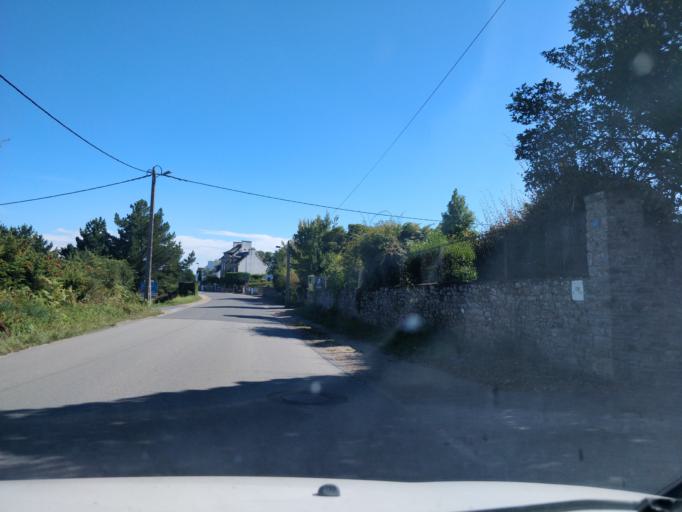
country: FR
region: Brittany
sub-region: Departement du Morbihan
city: Locmariaquer
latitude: 47.5739
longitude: -2.9501
